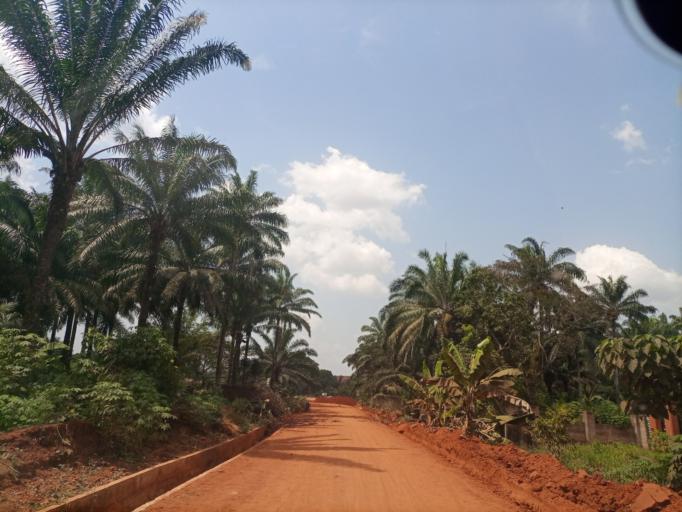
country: NG
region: Enugu
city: Obollo-Afor
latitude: 6.8693
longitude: 7.4713
